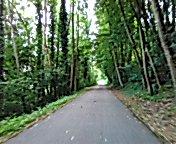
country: LU
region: Grevenmacher
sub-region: Canton d'Echternach
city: Rosport
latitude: 49.7779
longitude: 6.5105
